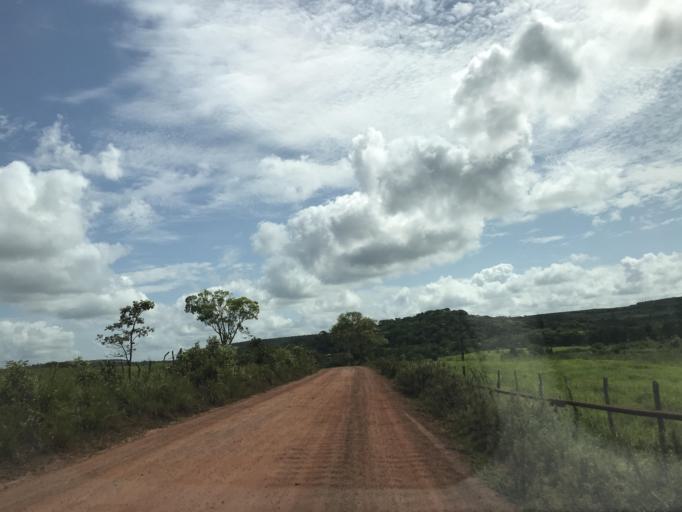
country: BR
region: Bahia
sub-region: Entre Rios
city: Entre Rios
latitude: -12.1653
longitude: -38.0816
